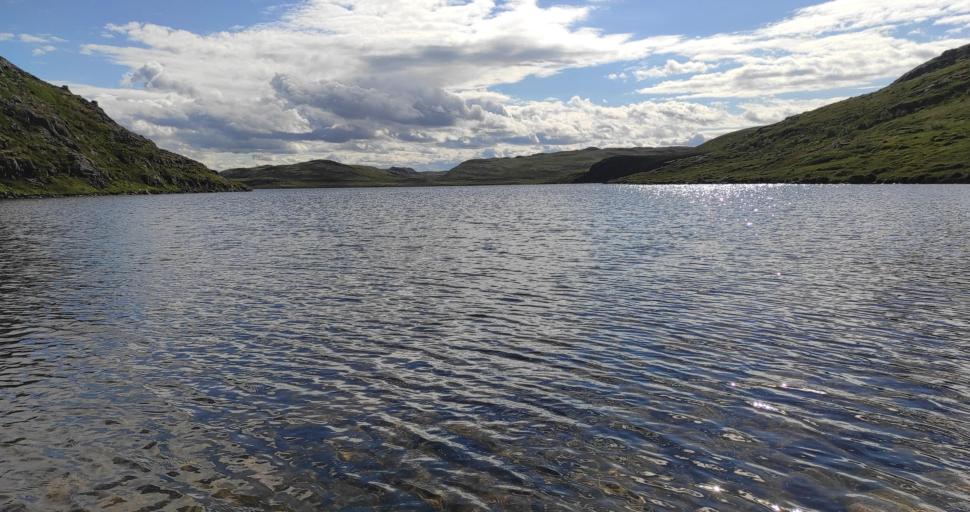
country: RU
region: Murmansk
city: Teriberka
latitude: 69.2029
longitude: 35.3862
